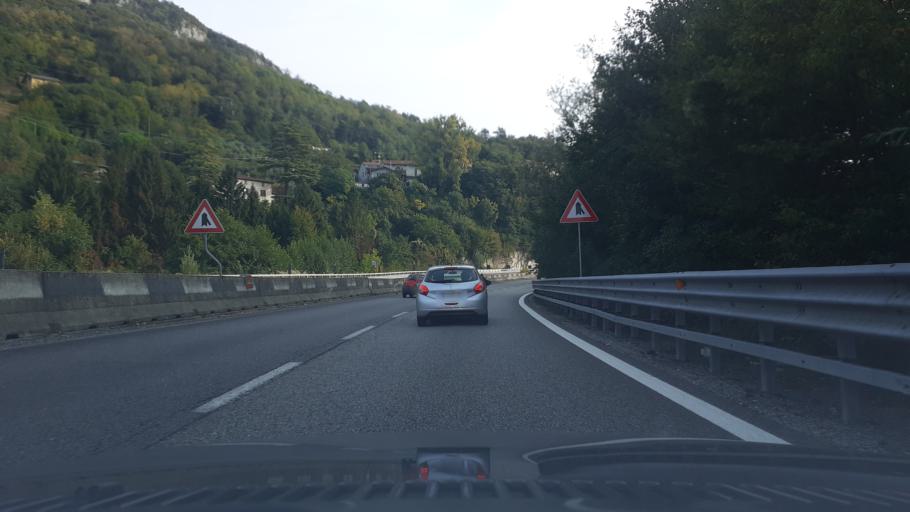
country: IT
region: Lombardy
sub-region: Provincia di Lecco
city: Suello
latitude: 45.8226
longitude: 9.3247
